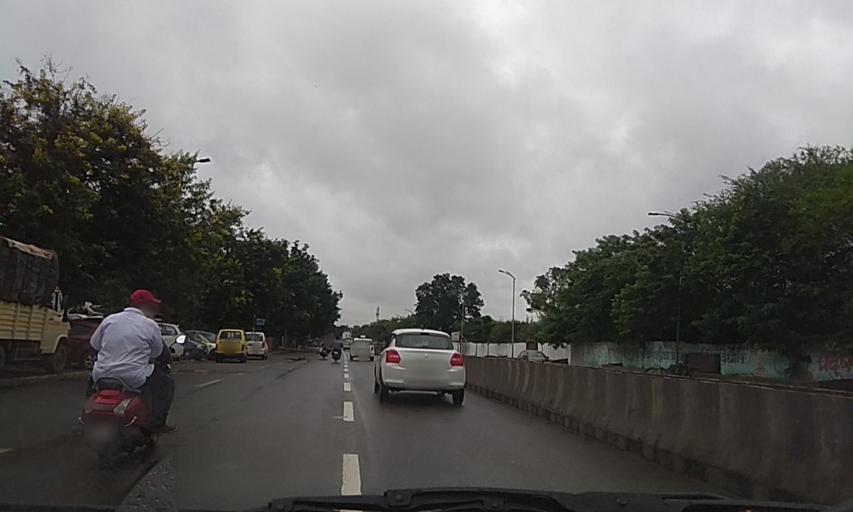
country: IN
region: Maharashtra
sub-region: Pune Division
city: Khadki
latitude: 18.5523
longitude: 73.8746
